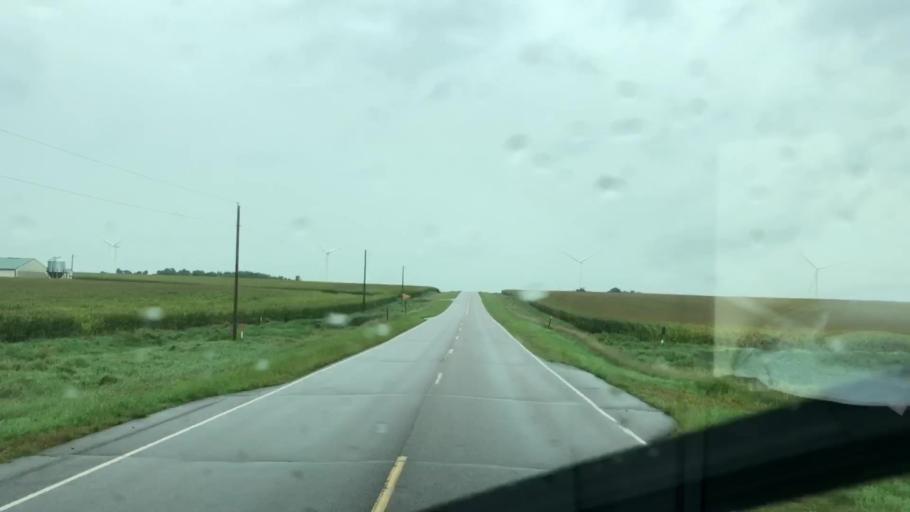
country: US
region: Iowa
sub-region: O'Brien County
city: Sanborn
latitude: 43.2085
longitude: -95.7233
